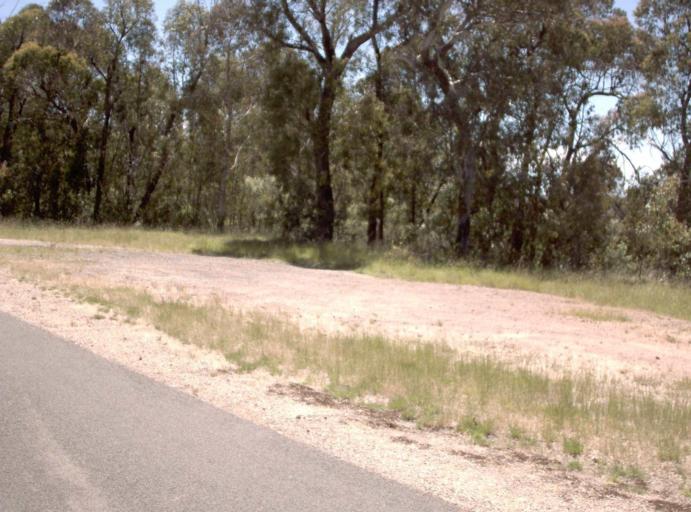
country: AU
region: New South Wales
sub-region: Snowy River
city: Jindabyne
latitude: -37.1106
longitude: 148.2514
